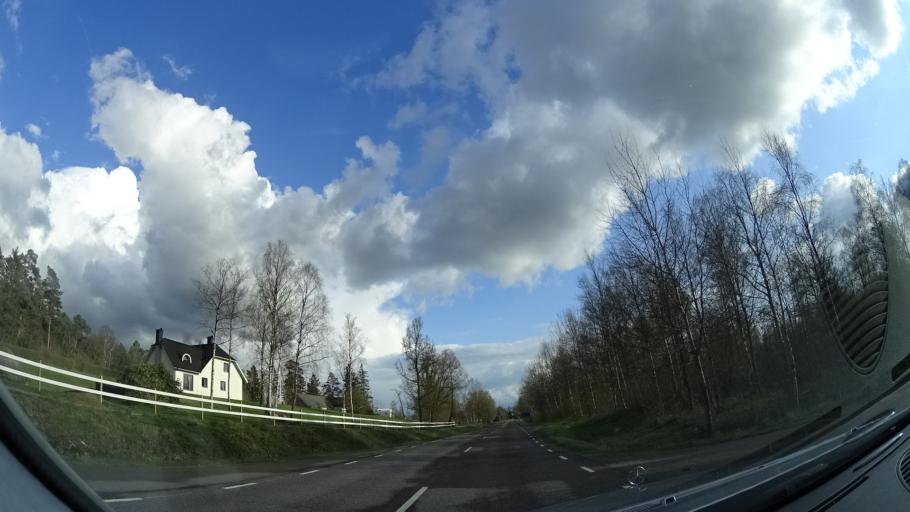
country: SE
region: Skane
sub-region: Perstorps Kommun
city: Perstorp
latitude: 56.1531
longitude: 13.3840
